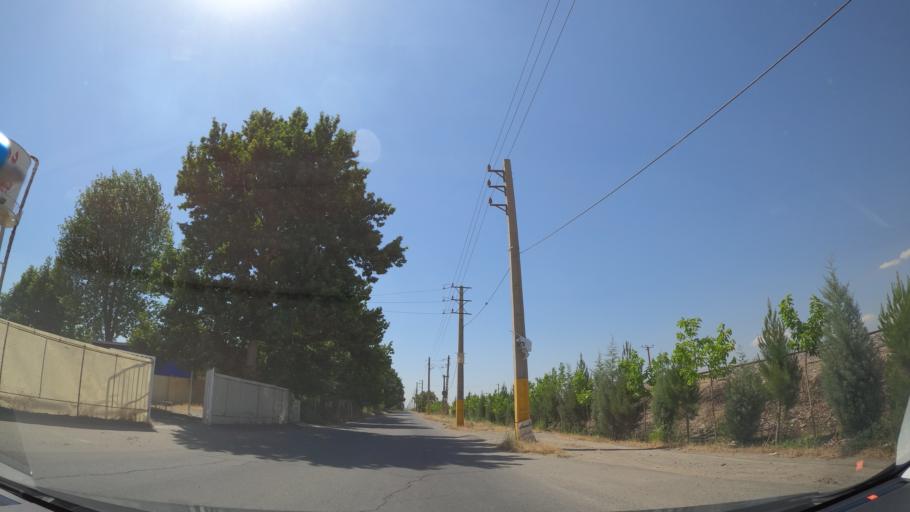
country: IR
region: Alborz
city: Hashtgerd
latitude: 35.9160
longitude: 50.7322
